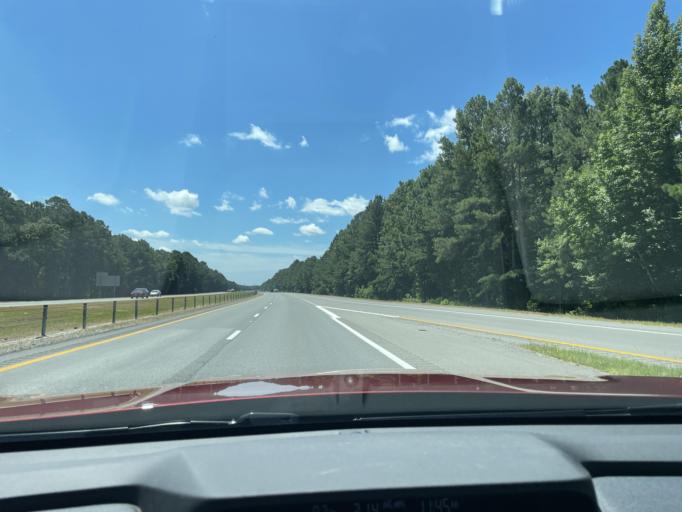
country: US
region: Arkansas
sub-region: Jefferson County
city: White Hall
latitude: 34.2834
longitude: -92.1176
